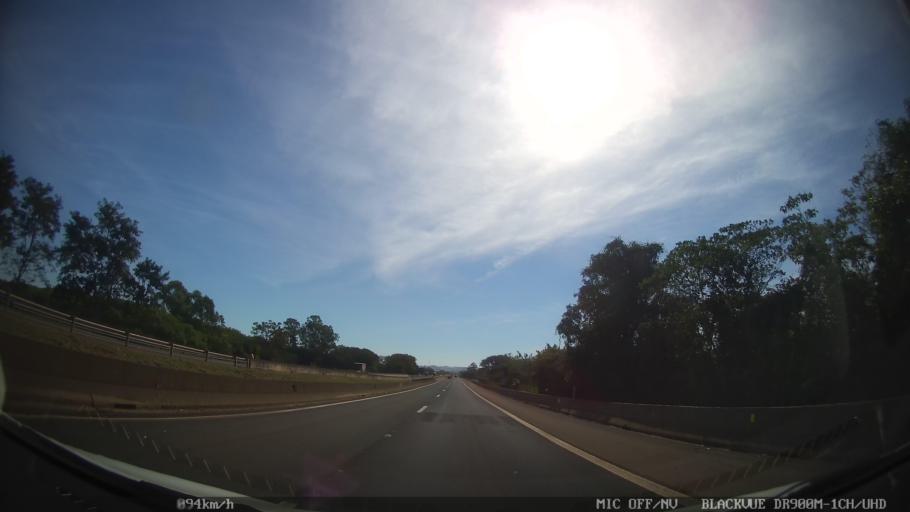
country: BR
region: Sao Paulo
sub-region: Porto Ferreira
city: Porto Ferreira
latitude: -21.8458
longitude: -47.4950
